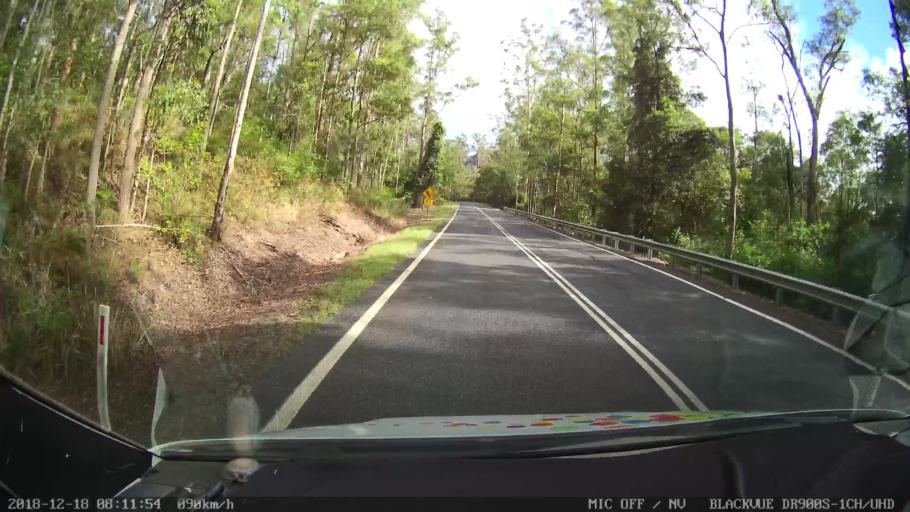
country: AU
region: New South Wales
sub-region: Kyogle
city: Kyogle
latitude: -28.3448
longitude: 152.6703
